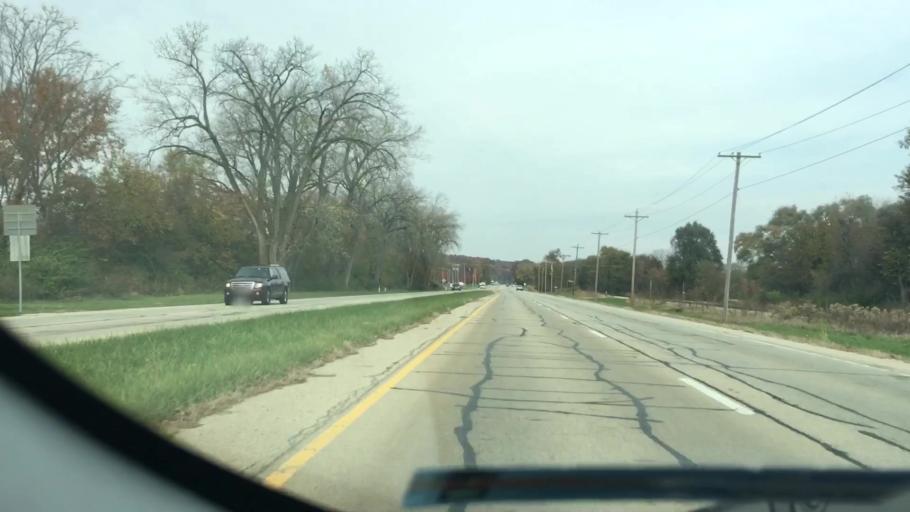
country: US
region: Illinois
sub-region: Peoria County
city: Peoria Heights
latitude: 40.7619
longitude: -89.5671
